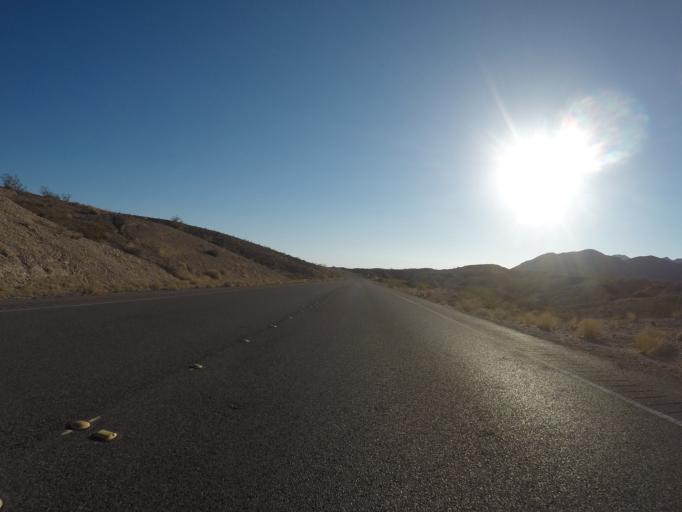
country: US
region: Nevada
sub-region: Clark County
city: Moapa Valley
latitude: 36.3992
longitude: -114.4225
